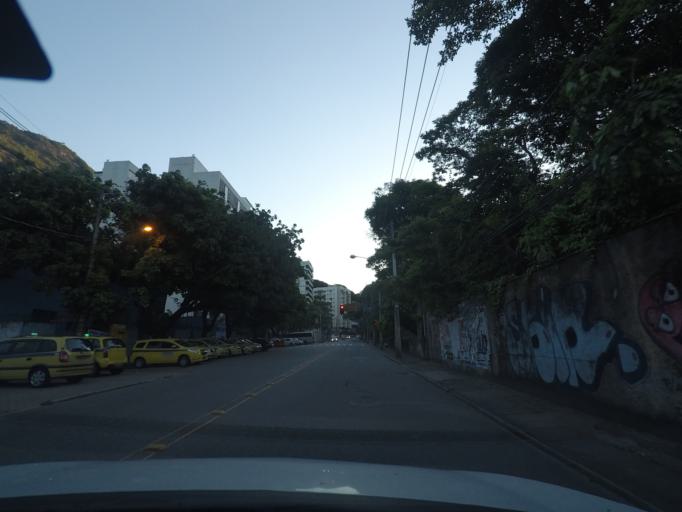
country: BR
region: Rio de Janeiro
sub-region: Rio De Janeiro
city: Rio de Janeiro
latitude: -22.9452
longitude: -43.2545
